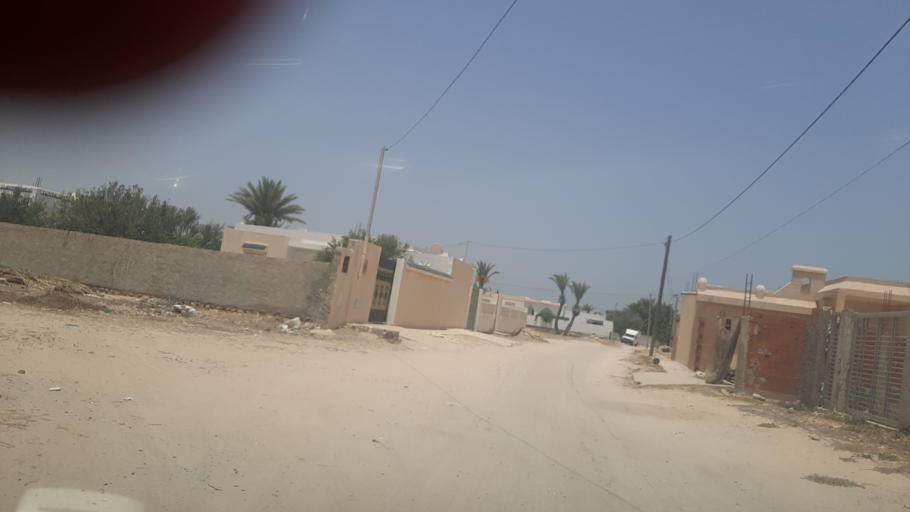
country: TN
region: Safaqis
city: Al Qarmadah
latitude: 34.6525
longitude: 11.0255
